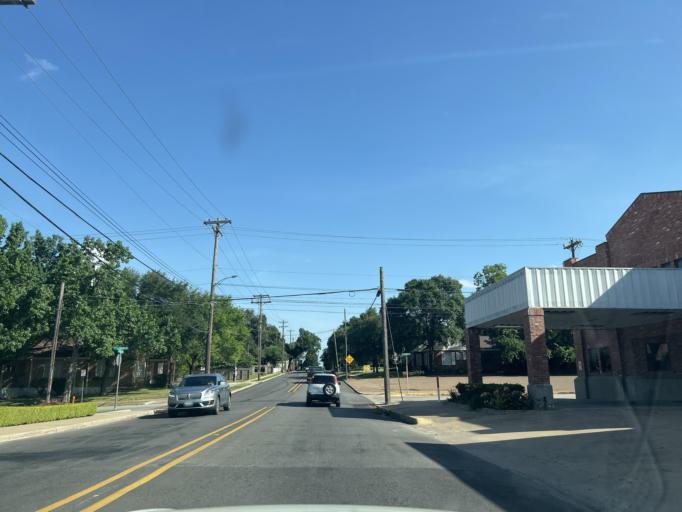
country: US
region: Texas
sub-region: Washington County
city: Brenham
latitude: 30.1637
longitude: -96.3993
